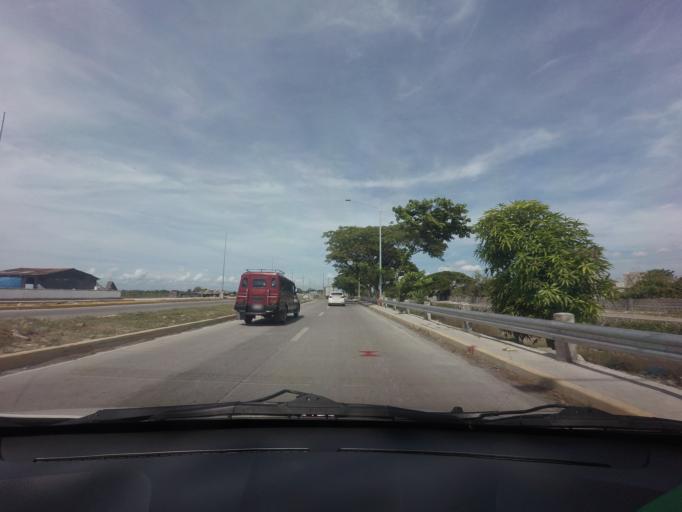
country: PH
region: Calabarzon
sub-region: Province of Rizal
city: Taguig
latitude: 14.5317
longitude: 121.0969
